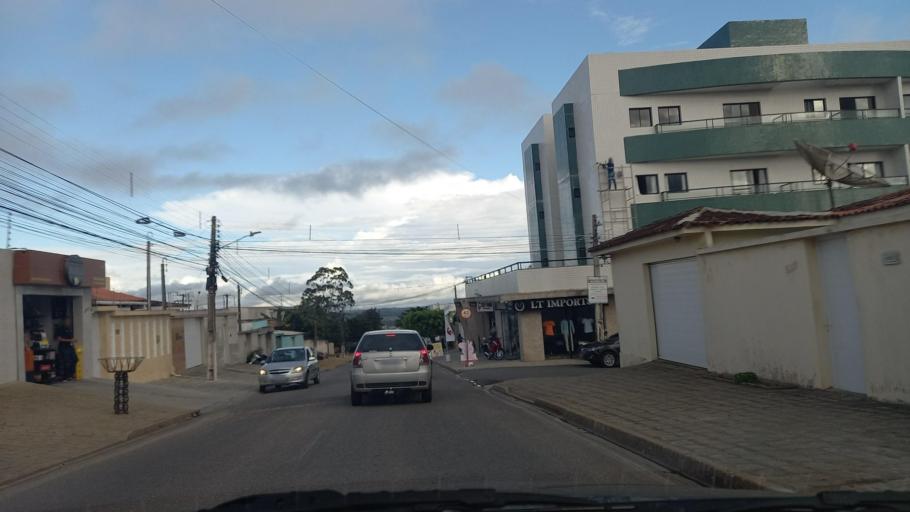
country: BR
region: Pernambuco
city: Garanhuns
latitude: -8.9040
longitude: -36.4910
